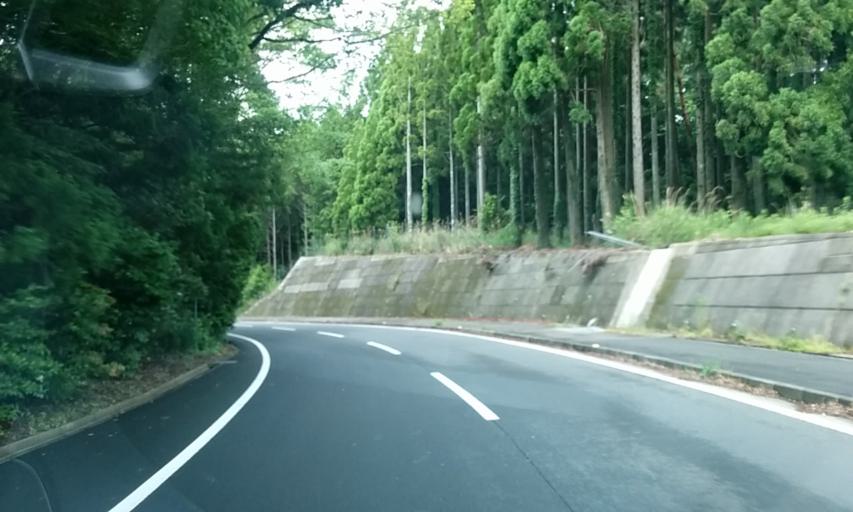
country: JP
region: Kyoto
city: Kameoka
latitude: 35.0132
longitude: 135.4395
